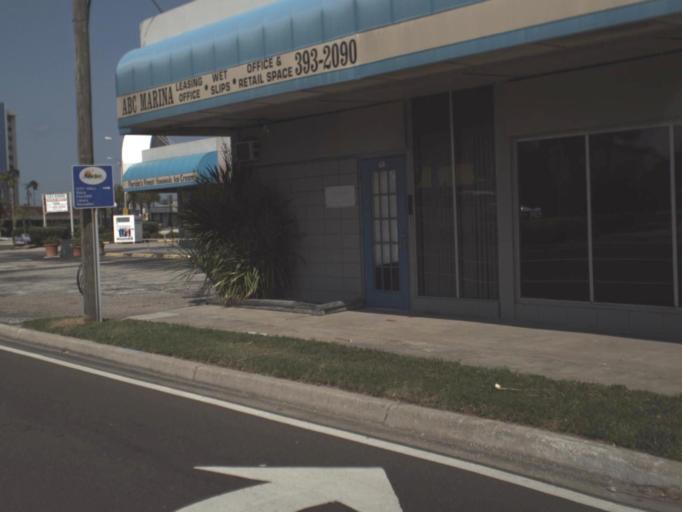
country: US
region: Florida
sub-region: Pinellas County
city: Madeira Beach
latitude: 27.8025
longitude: -82.7996
